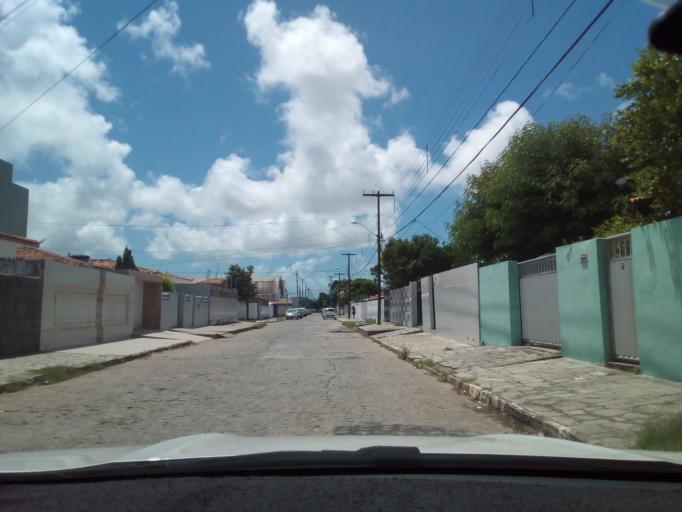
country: BR
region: Paraiba
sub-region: Joao Pessoa
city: Joao Pessoa
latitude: -7.1665
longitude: -34.8706
